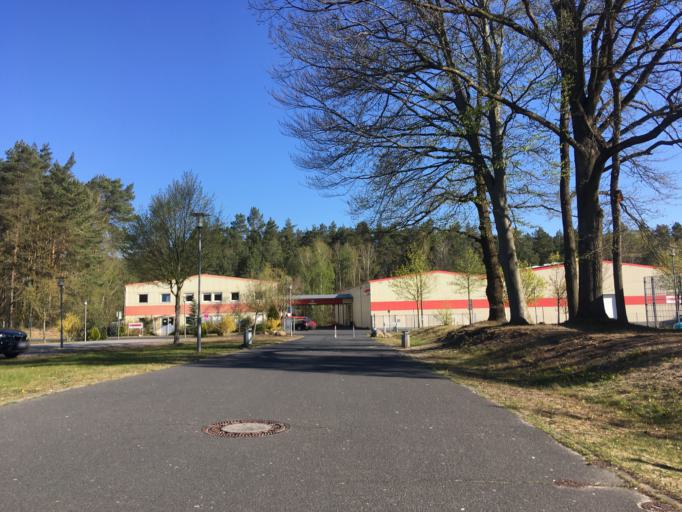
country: DE
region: Brandenburg
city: Bernau bei Berlin
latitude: 52.7076
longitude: 13.5427
